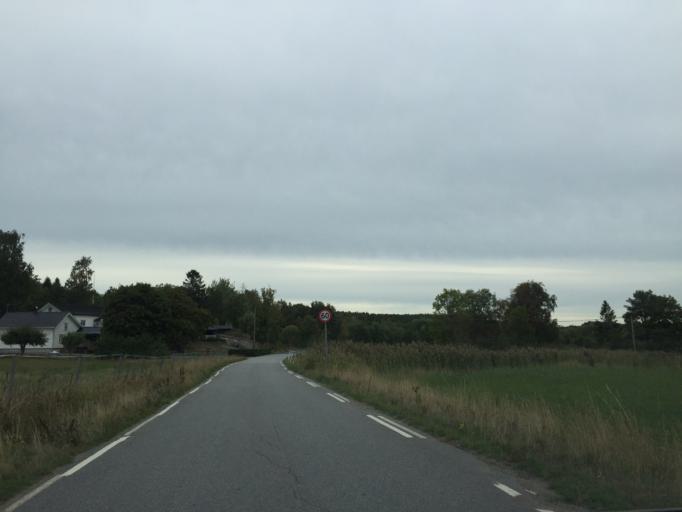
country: NO
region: Ostfold
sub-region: Hvaler
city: Skjaerhalden
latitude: 59.0635
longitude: 11.0333
